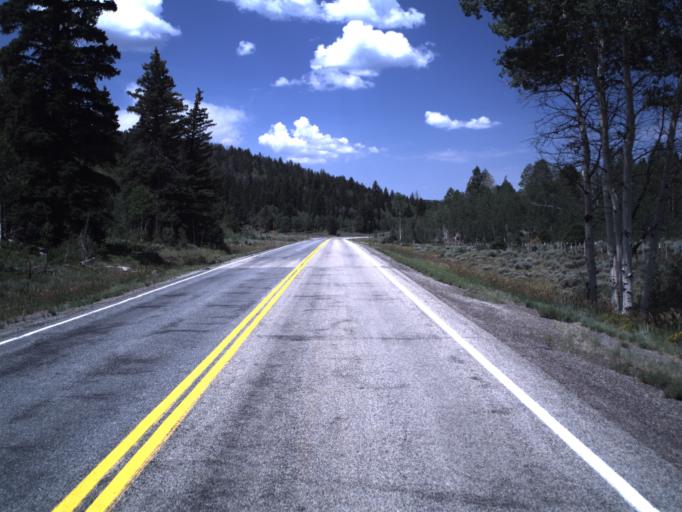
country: US
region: Utah
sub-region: Carbon County
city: Helper
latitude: 39.8584
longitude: -111.1015
